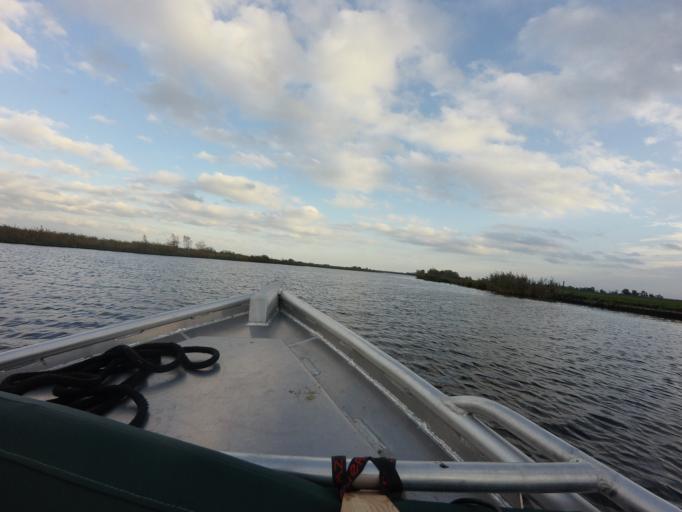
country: NL
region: Overijssel
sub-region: Gemeente Steenwijkerland
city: Blokzijl
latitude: 52.7335
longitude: 5.9807
